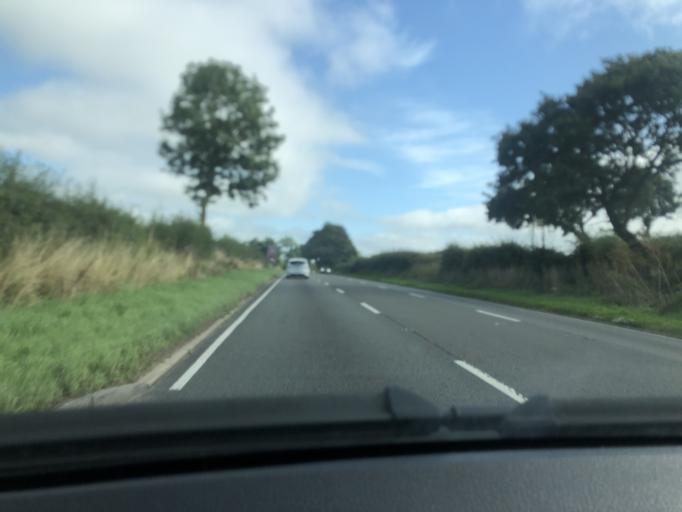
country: GB
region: England
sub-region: Devon
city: Honiton
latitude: 50.8103
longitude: -3.1708
